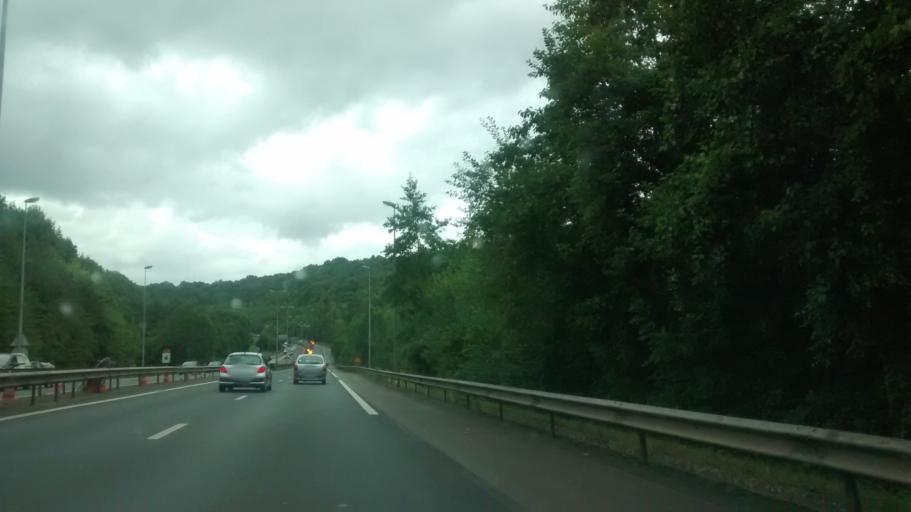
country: FR
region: Haute-Normandie
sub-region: Departement de la Seine-Maritime
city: Darnetal
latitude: 49.4544
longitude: 1.1447
